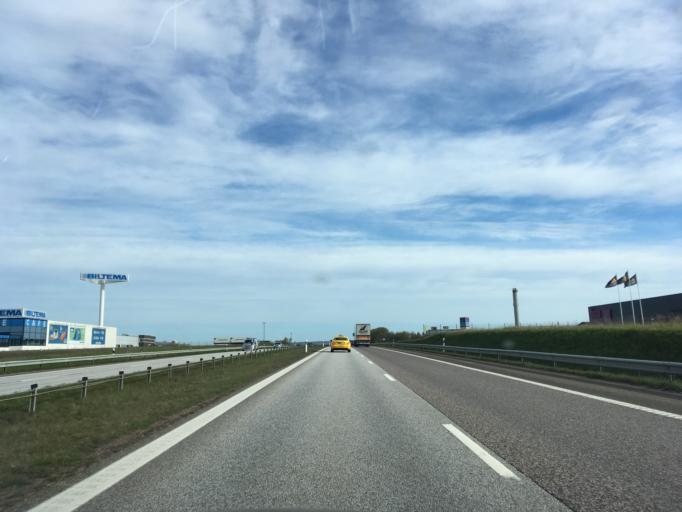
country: SE
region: Skane
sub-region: Angelholms Kommun
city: AEngelholm
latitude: 56.2419
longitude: 12.8989
